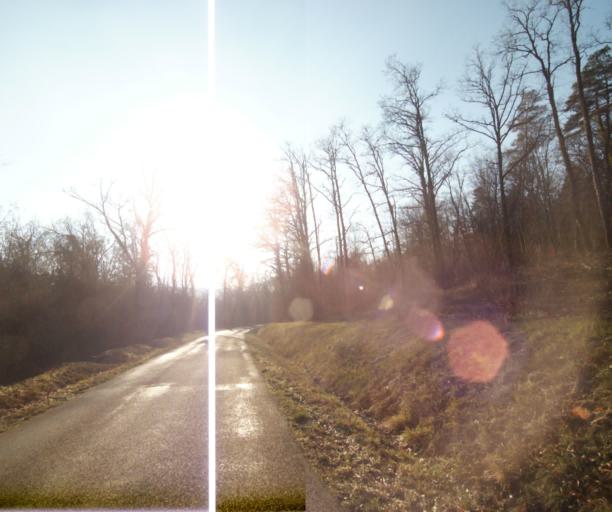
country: FR
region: Champagne-Ardenne
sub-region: Departement de la Haute-Marne
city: Chevillon
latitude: 48.5449
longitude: 5.1231
